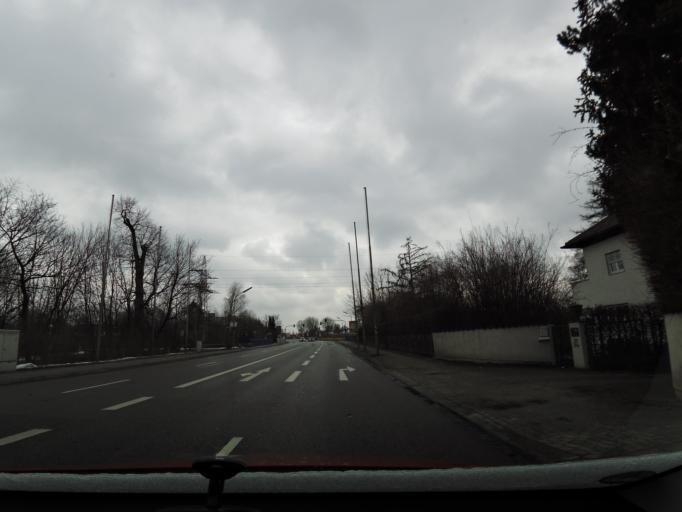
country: DE
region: Bavaria
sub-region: Upper Bavaria
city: Unterfoehring
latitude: 48.1837
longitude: 11.6334
